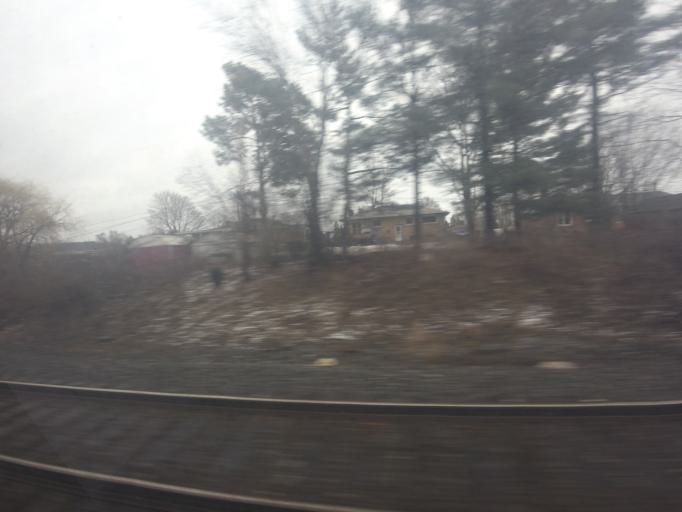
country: CA
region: Ontario
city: Kingston
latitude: 44.2326
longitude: -76.6293
